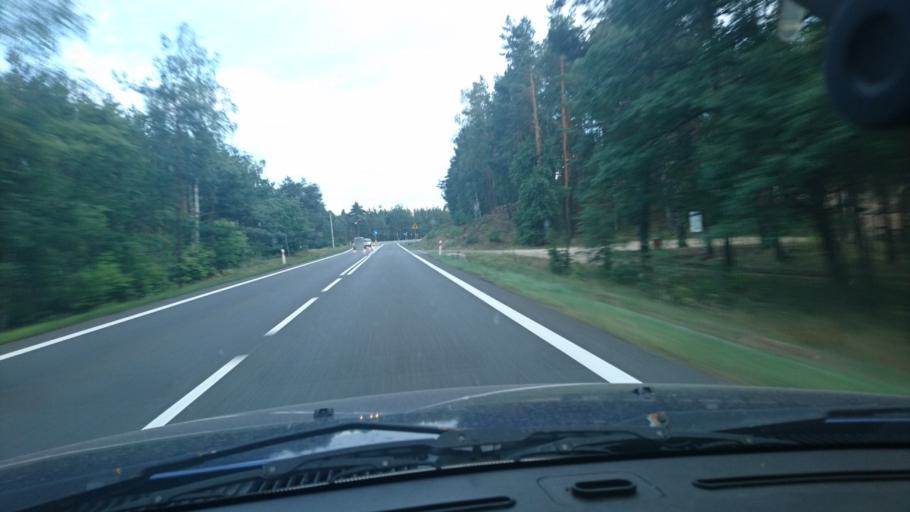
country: PL
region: Silesian Voivodeship
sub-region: Powiat tarnogorski
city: Tworog
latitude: 50.5996
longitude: 18.7020
